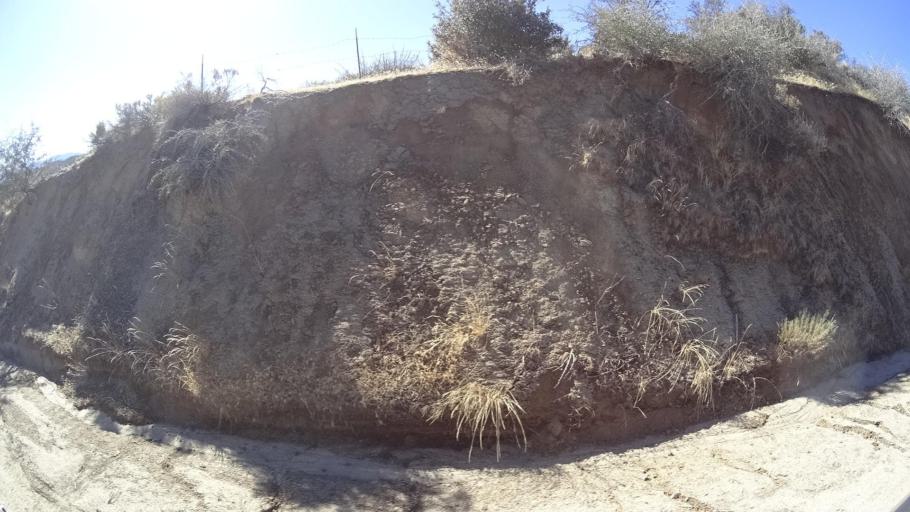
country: US
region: California
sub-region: Kern County
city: Wofford Heights
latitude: 35.7076
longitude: -118.5039
